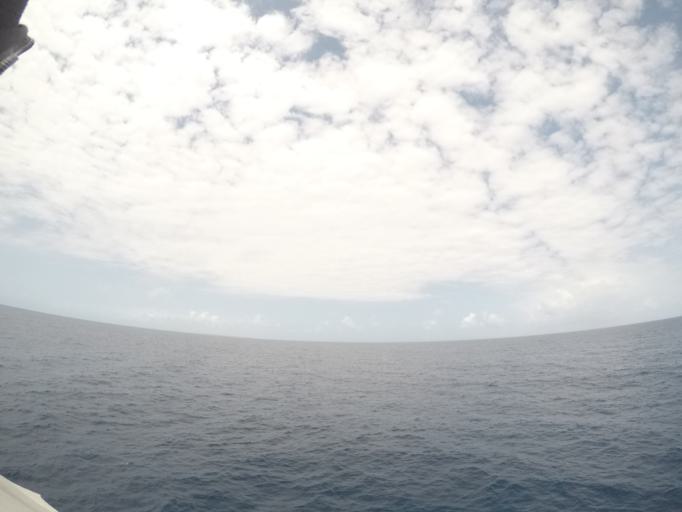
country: TZ
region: Zanzibar North
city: Nungwi
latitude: -5.6073
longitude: 39.3357
